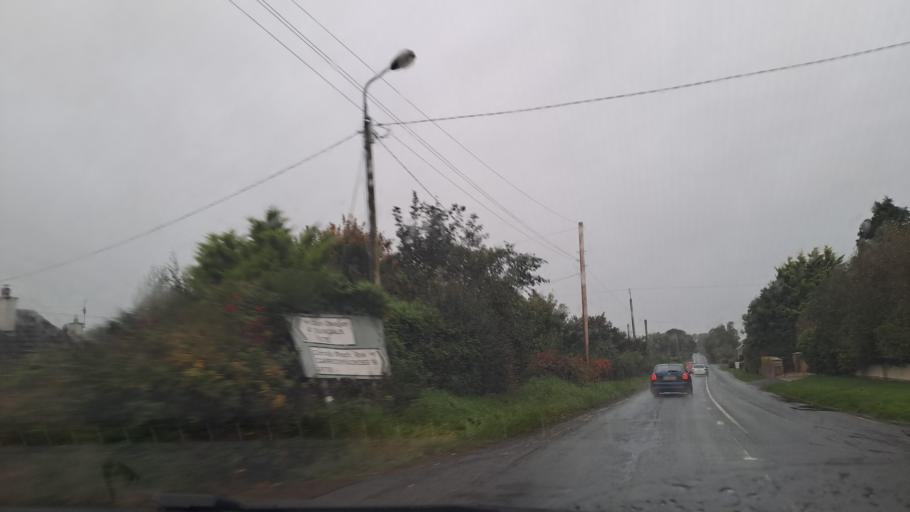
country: IE
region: Leinster
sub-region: Lu
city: Dundalk
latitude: 53.9941
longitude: -6.4481
